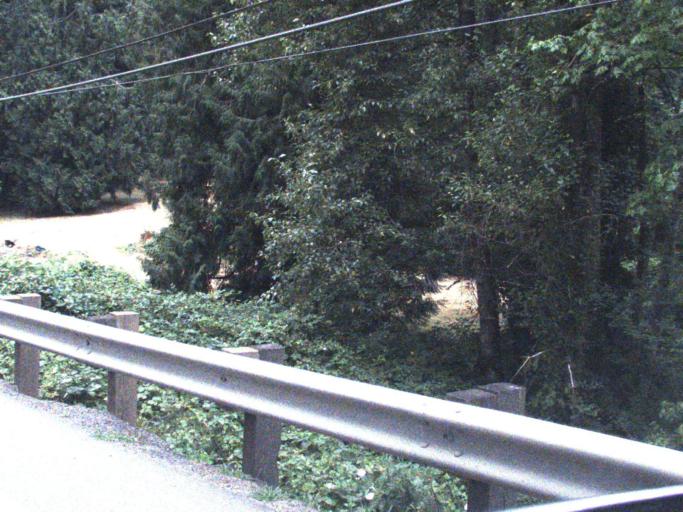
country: US
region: Washington
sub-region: King County
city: Fall City
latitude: 47.5670
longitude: -121.8720
